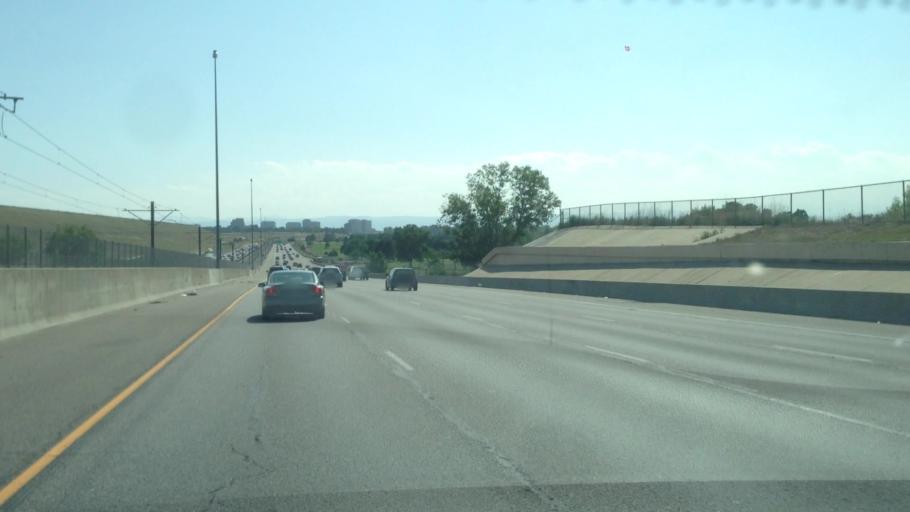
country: US
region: Colorado
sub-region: Arapahoe County
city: Centennial
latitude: 39.6540
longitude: -104.8554
